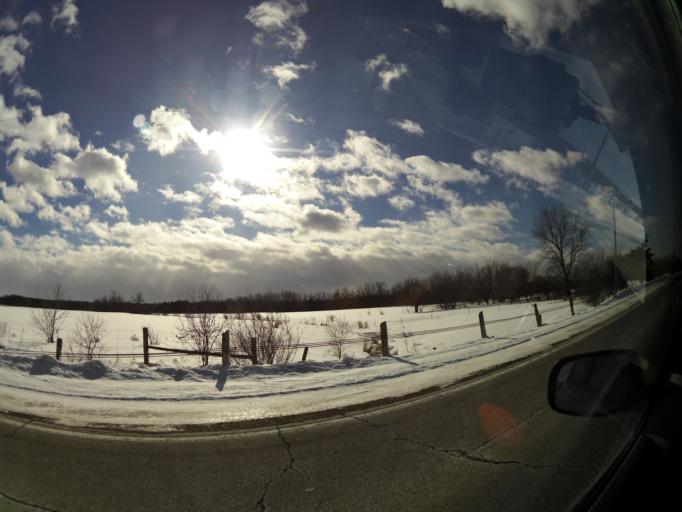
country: CA
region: Ontario
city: Ottawa
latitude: 45.3776
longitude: -75.5568
